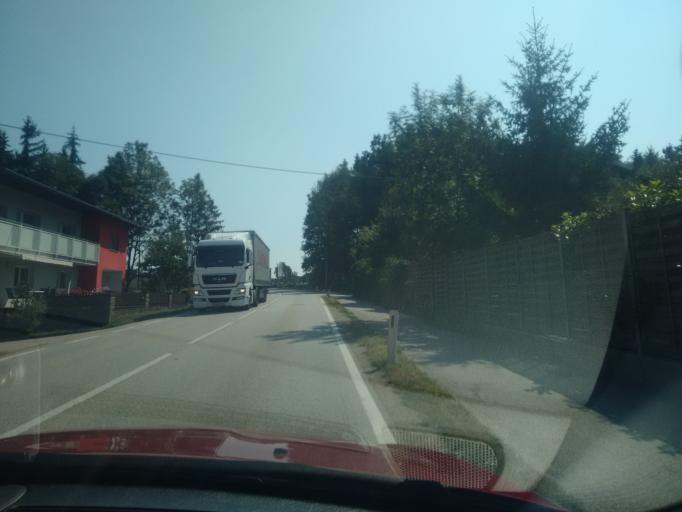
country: AT
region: Upper Austria
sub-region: Wels-Land
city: Sattledt
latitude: 48.0759
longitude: 14.0435
